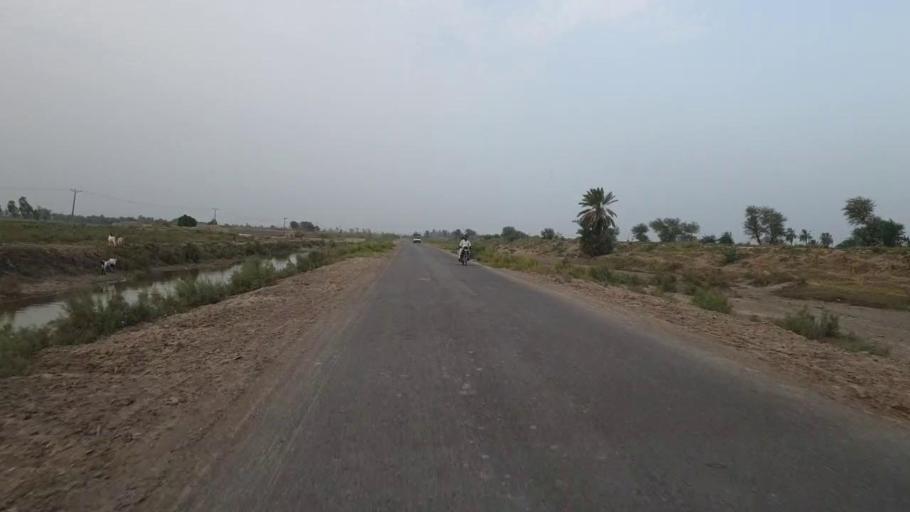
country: PK
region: Sindh
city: Daur
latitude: 26.4474
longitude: 68.2848
